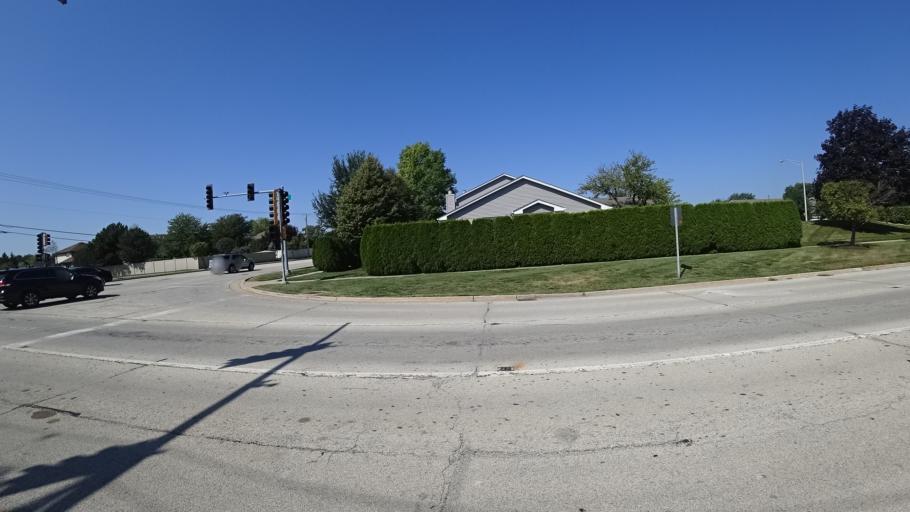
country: US
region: Illinois
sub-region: Cook County
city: Orland Park
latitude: 41.6313
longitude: -87.8196
